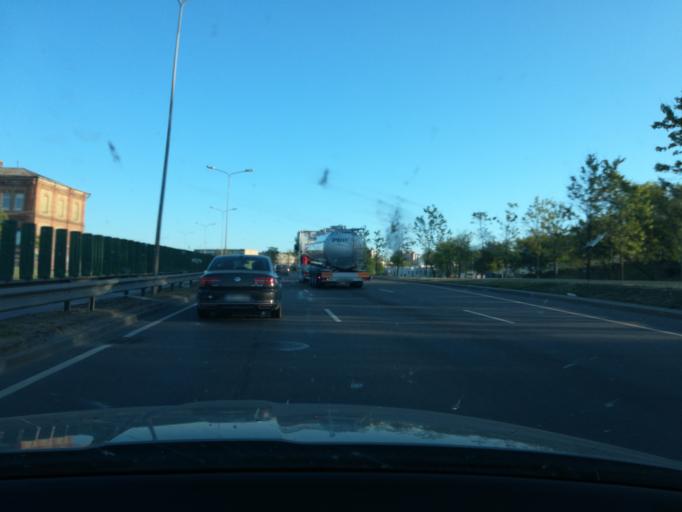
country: LT
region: Vilnius County
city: Vilkpede
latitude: 54.6642
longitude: 25.2551
